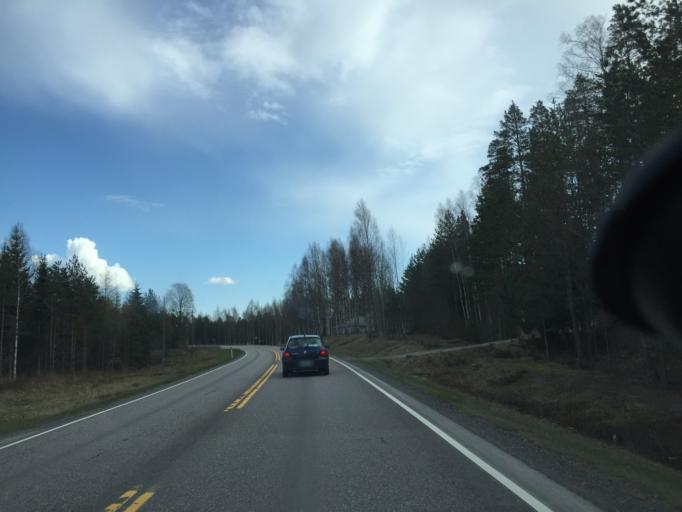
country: FI
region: Uusimaa
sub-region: Raaseporin
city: Ekenaes
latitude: 60.0192
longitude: 23.3787
